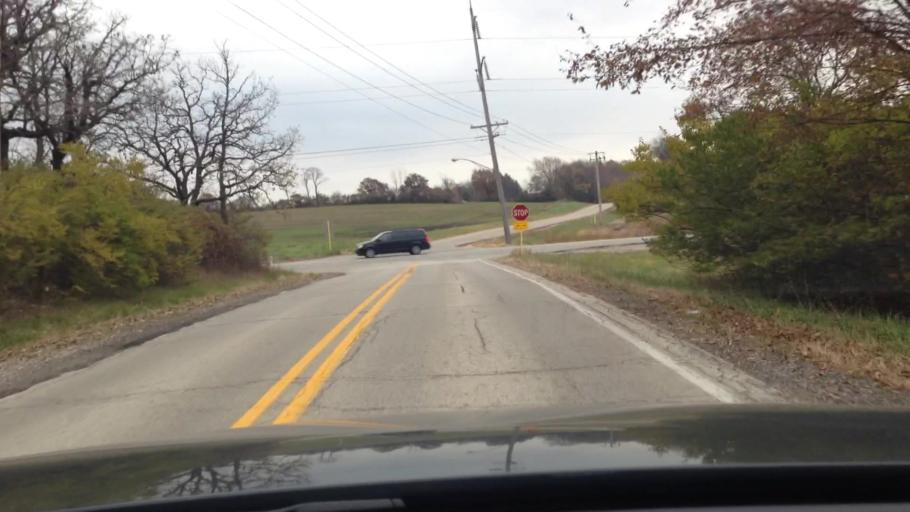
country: US
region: Illinois
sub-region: McHenry County
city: Woodstock
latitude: 42.2711
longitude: -88.4338
